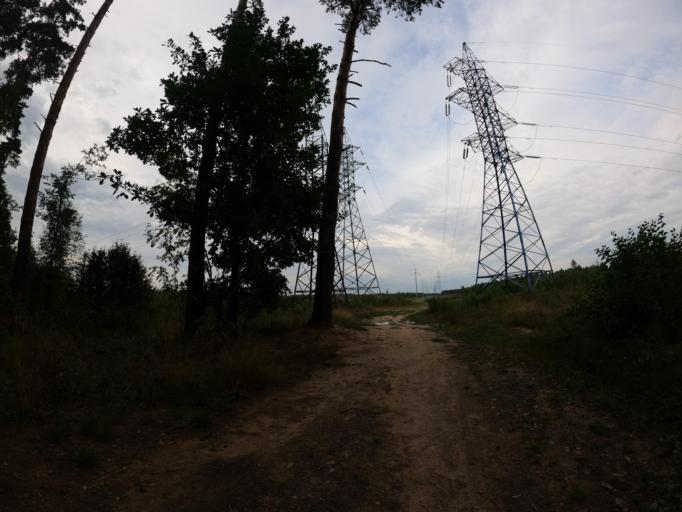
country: RU
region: Moskovskaya
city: Rodniki
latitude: 55.6686
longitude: 38.0788
